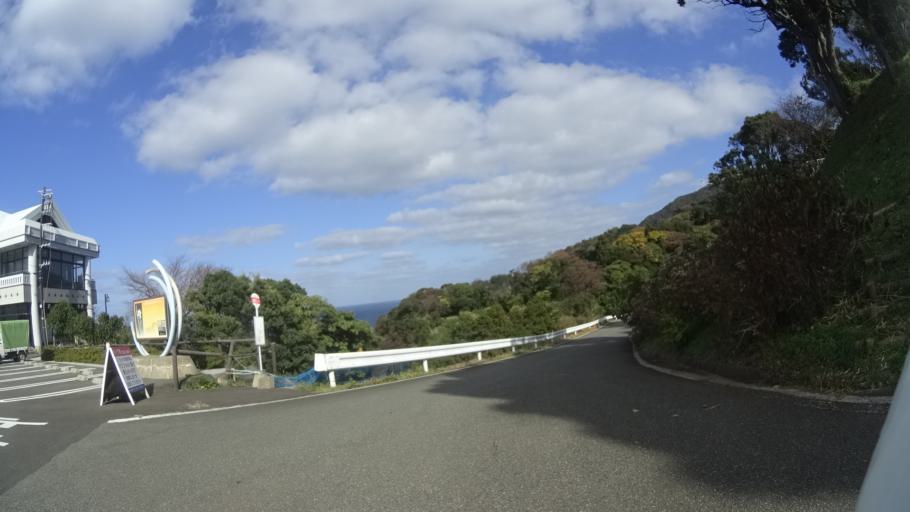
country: JP
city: Asahi
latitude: 35.9820
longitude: 135.9615
